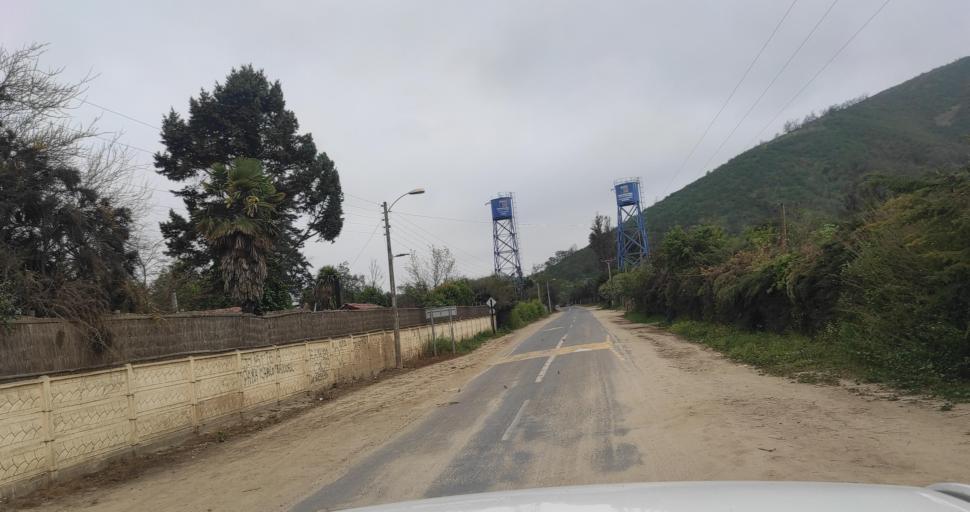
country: CL
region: Valparaiso
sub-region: Provincia de Marga Marga
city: Villa Alemana
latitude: -33.3576
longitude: -71.3028
